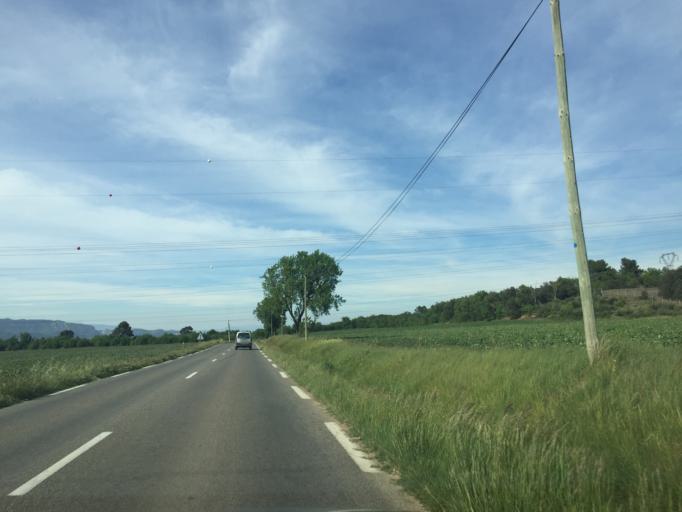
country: FR
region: Provence-Alpes-Cote d'Azur
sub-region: Departement du Var
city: Vinon-sur-Verdon
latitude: 43.7725
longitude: 5.8145
